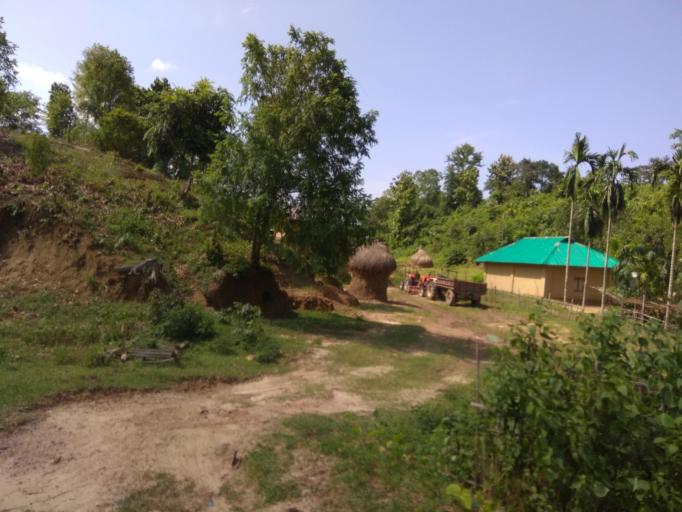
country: BD
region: Chittagong
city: Khagrachhari
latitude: 23.0354
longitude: 92.0066
